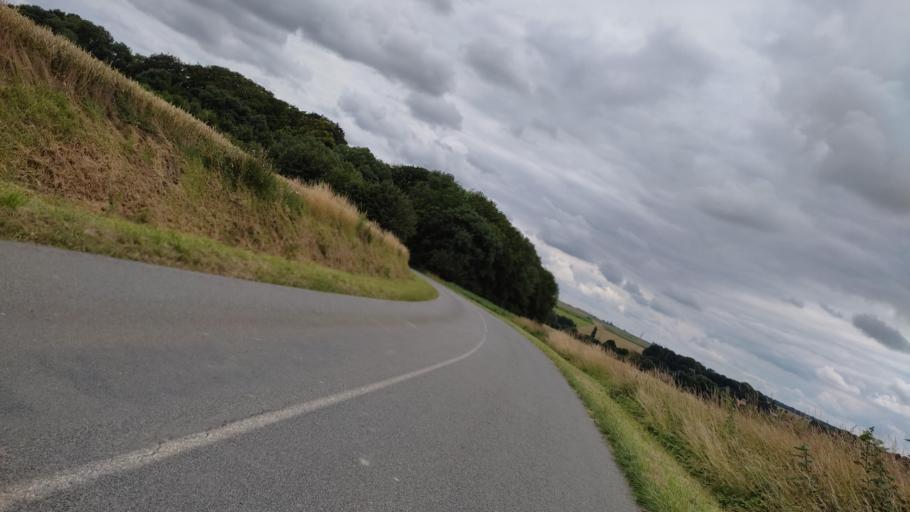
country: FR
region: Nord-Pas-de-Calais
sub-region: Departement du Pas-de-Calais
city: Beaumetz-les-Loges
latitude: 50.2376
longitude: 2.6752
